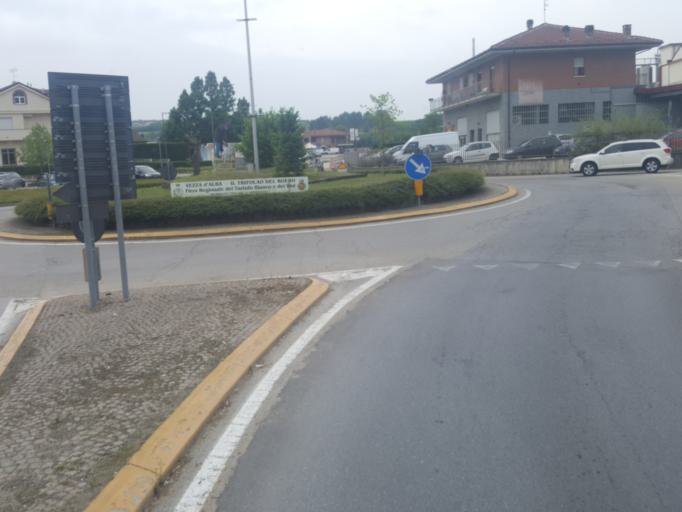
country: IT
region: Piedmont
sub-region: Provincia di Cuneo
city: Vezza d'Alba
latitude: 44.7614
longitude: 8.0094
